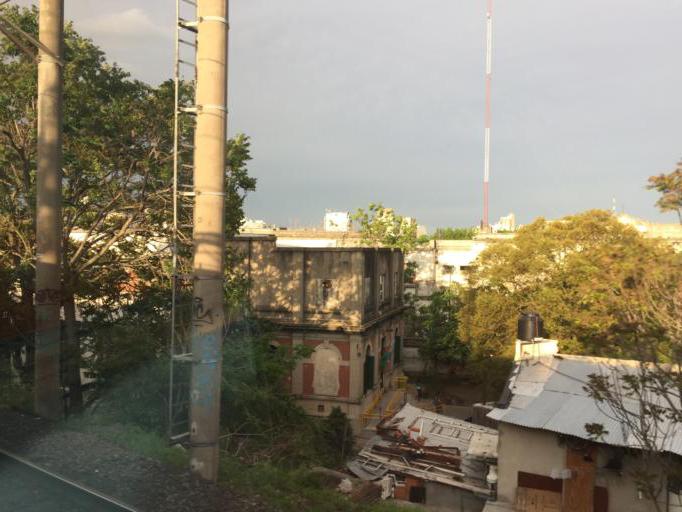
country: AR
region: Buenos Aires
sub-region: Partido de Avellaneda
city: Avellaneda
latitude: -34.6420
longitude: -58.3807
